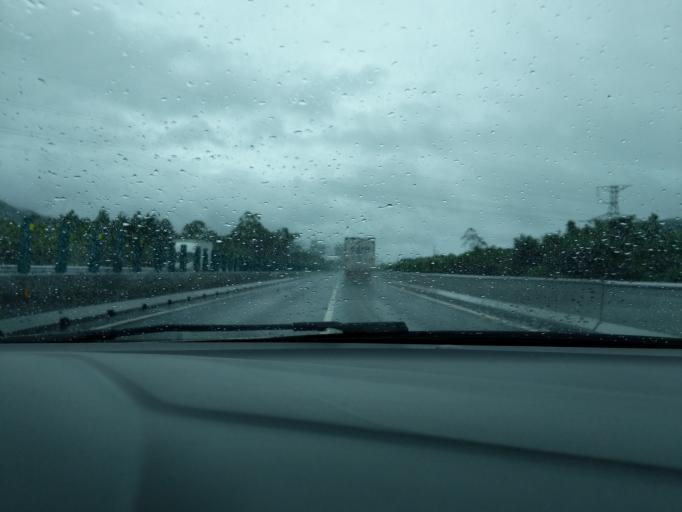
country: CN
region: Guangdong
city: Pingshi
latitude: 22.2498
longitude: 112.3066
